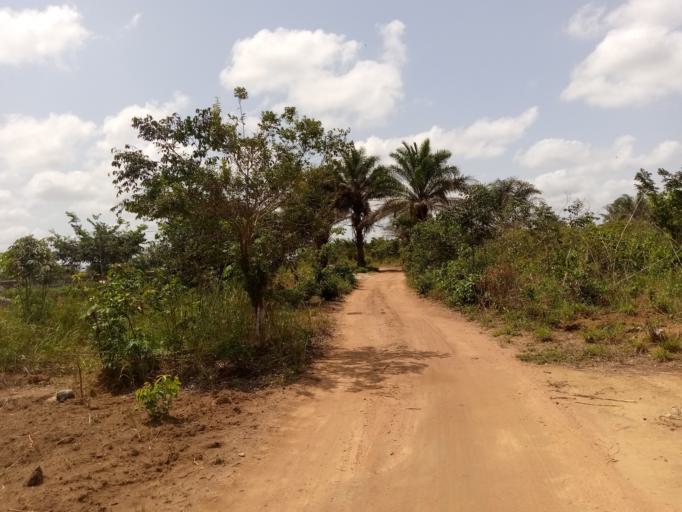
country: SL
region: Western Area
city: Waterloo
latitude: 8.3555
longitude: -13.0058
